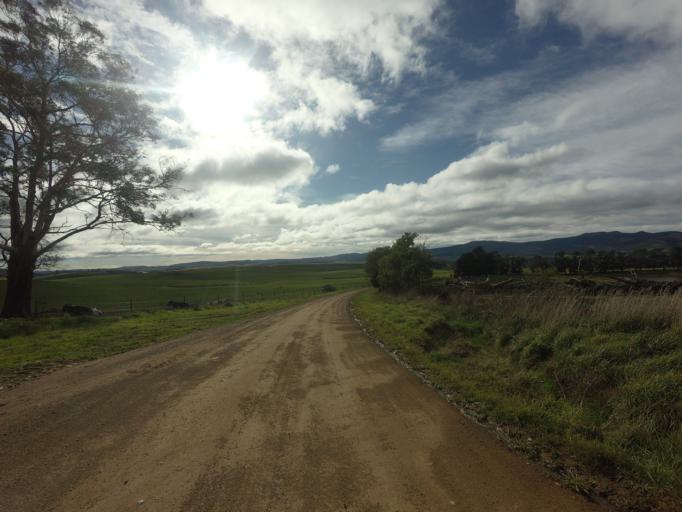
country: AU
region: Tasmania
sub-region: Derwent Valley
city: New Norfolk
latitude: -42.7189
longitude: 146.8744
